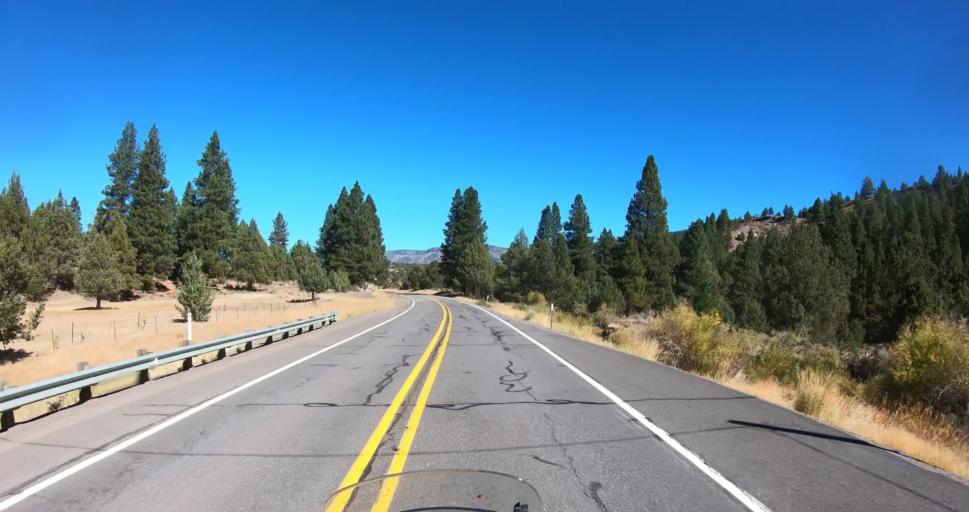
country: US
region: Oregon
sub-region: Lake County
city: Lakeview
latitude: 42.3965
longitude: -120.2952
